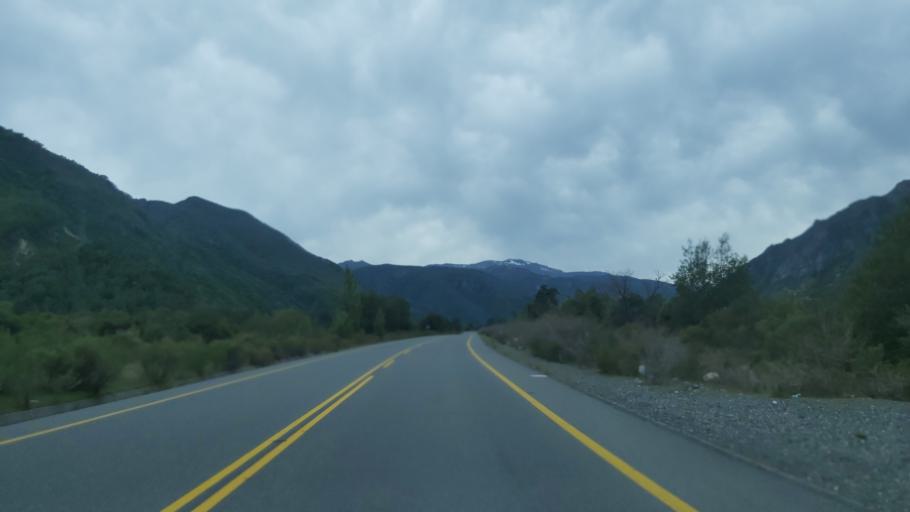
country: CL
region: Maule
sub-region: Provincia de Linares
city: Colbun
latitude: -35.7105
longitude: -71.0663
